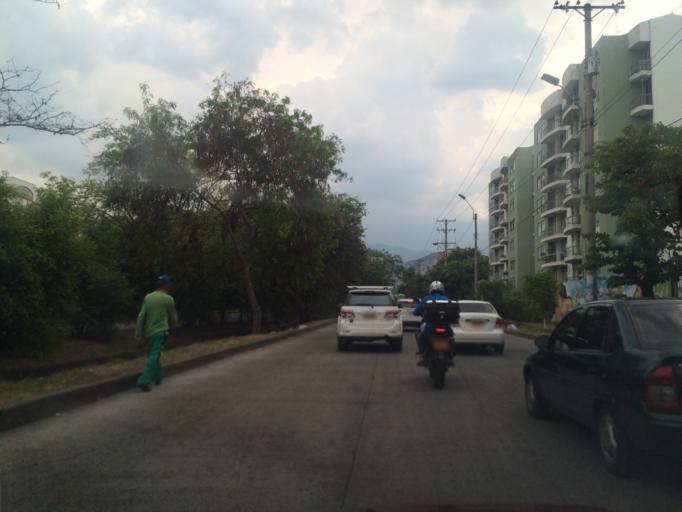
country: CO
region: Valle del Cauca
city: Cali
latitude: 3.3865
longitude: -76.5420
